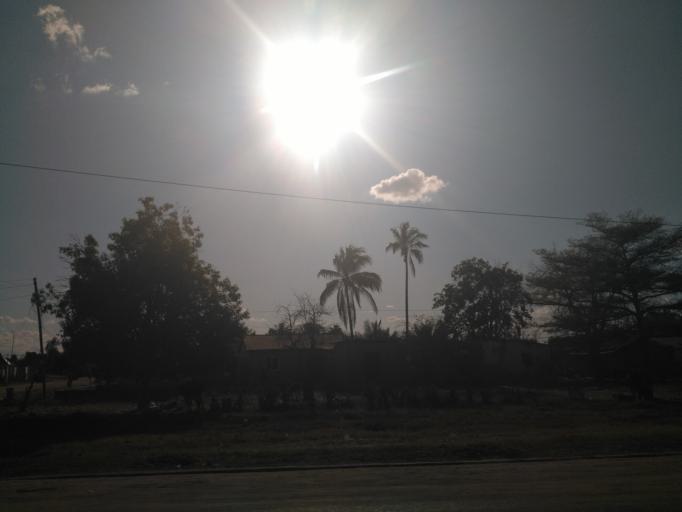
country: TZ
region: Dodoma
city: Dodoma
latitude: -6.1524
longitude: 35.7476
